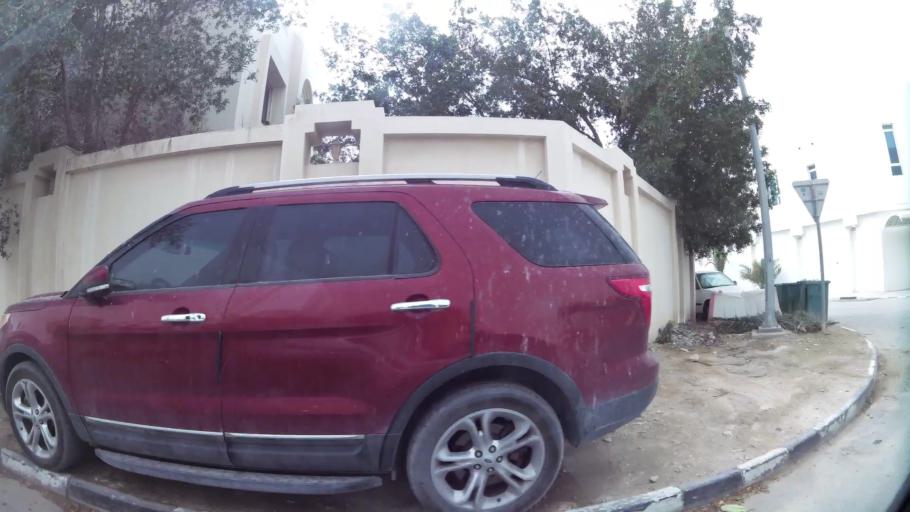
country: QA
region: Baladiyat ad Dawhah
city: Doha
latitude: 25.2416
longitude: 51.5315
